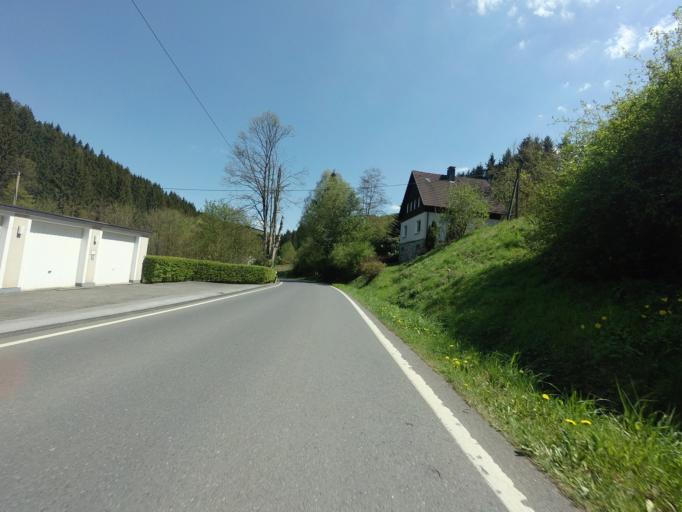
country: DE
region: North Rhine-Westphalia
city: Hemer
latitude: 51.3436
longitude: 7.7866
